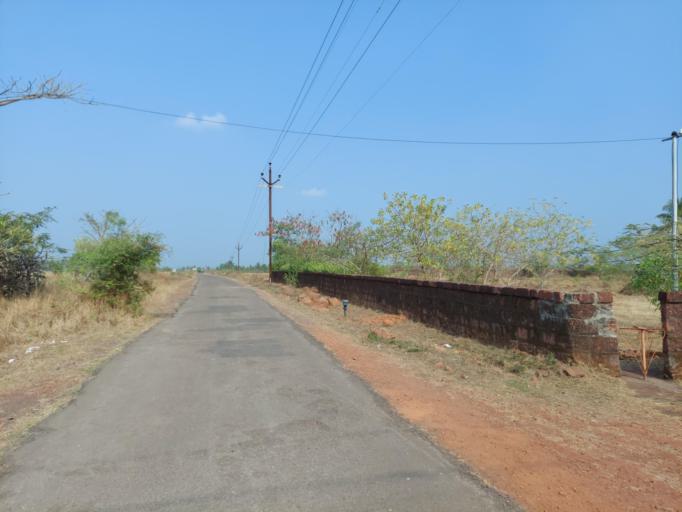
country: IN
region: Maharashtra
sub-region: Ratnagiri
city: Ratnagiri
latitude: 16.9280
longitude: 73.3209
